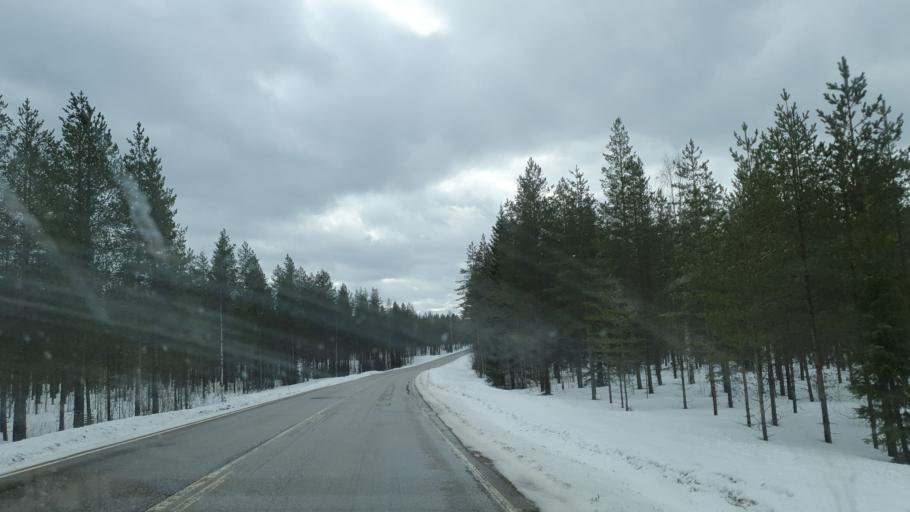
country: FI
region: Kainuu
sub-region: Kehys-Kainuu
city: Puolanka
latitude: 65.0521
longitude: 27.7164
